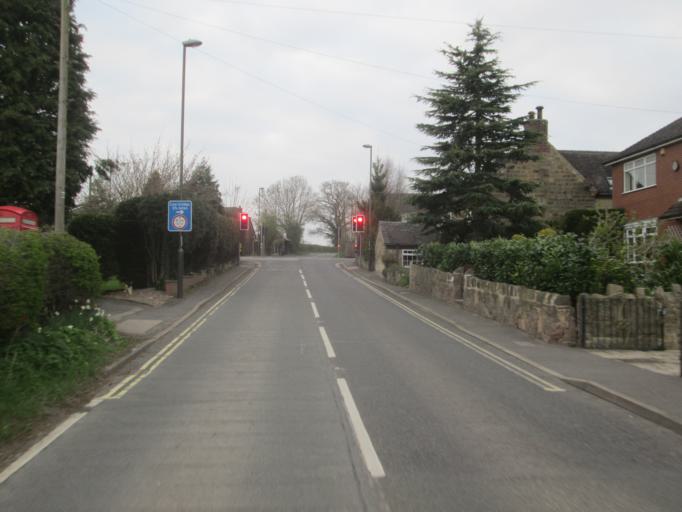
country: GB
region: England
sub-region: Derbyshire
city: Belper
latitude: 53.0187
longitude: -1.5440
